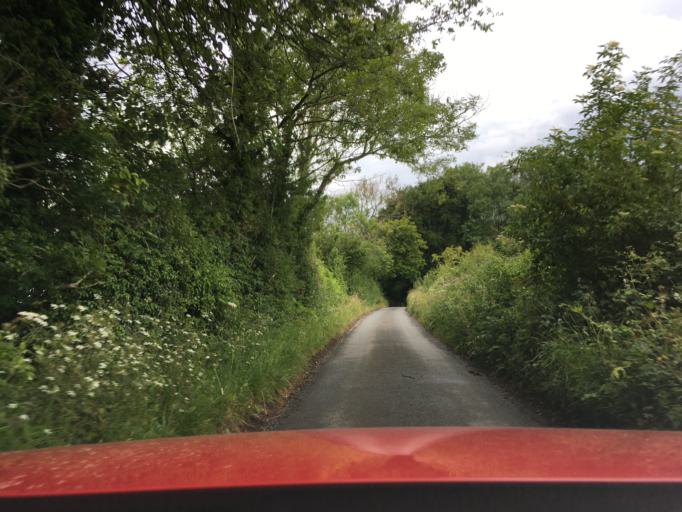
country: GB
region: England
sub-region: Gloucestershire
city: Shurdington
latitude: 51.8016
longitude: -2.0827
